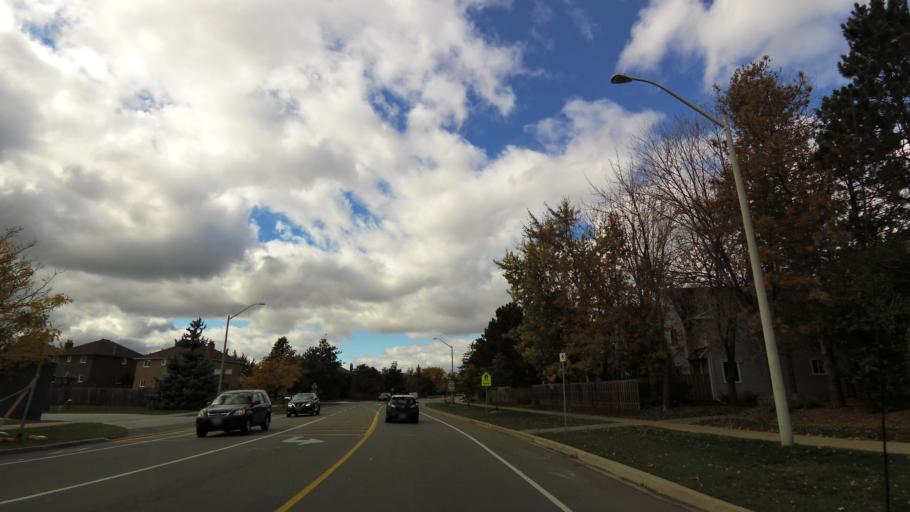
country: CA
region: Ontario
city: Oakville
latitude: 43.4666
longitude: -79.7117
